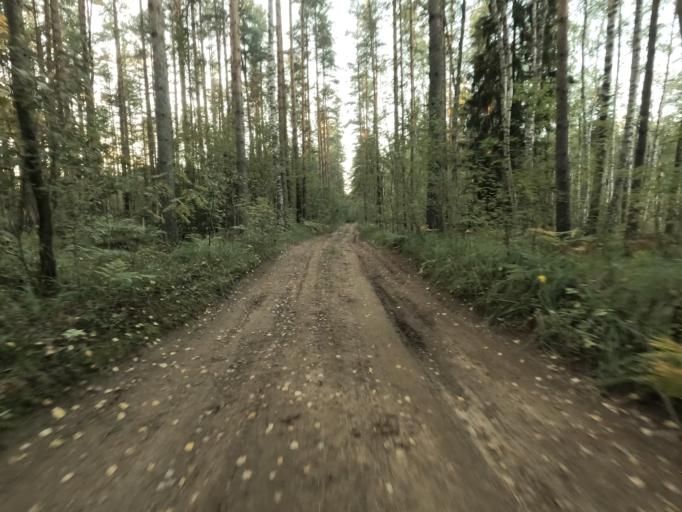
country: RU
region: Leningrad
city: Otradnoye
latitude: 59.8383
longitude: 30.8051
